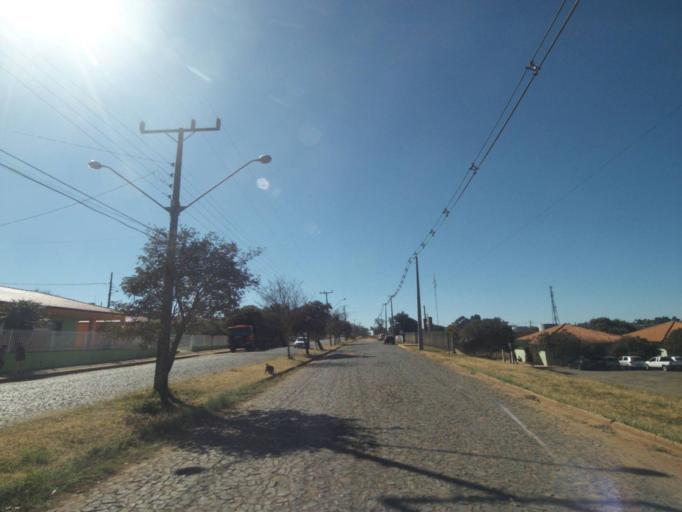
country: BR
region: Parana
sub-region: Reserva
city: Reserva
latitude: -24.6240
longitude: -50.6410
